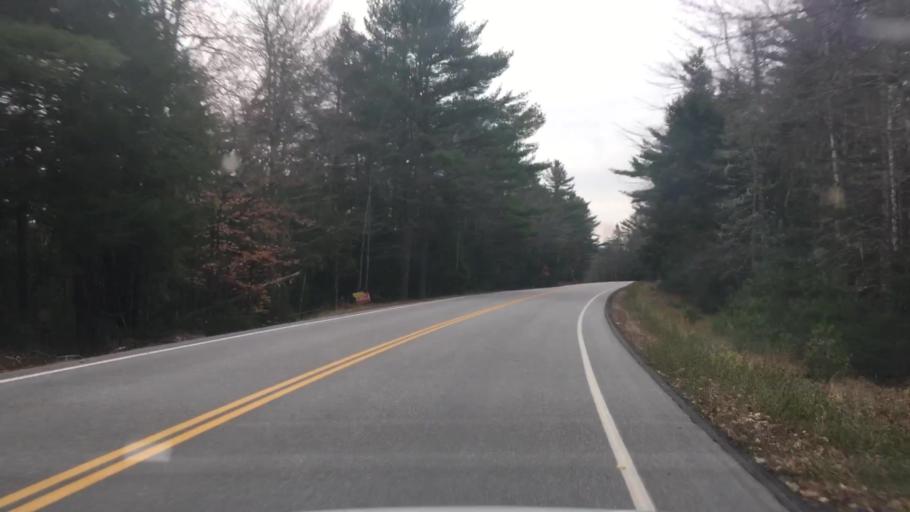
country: US
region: Maine
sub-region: Hancock County
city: Penobscot
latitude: 44.5076
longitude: -68.6557
